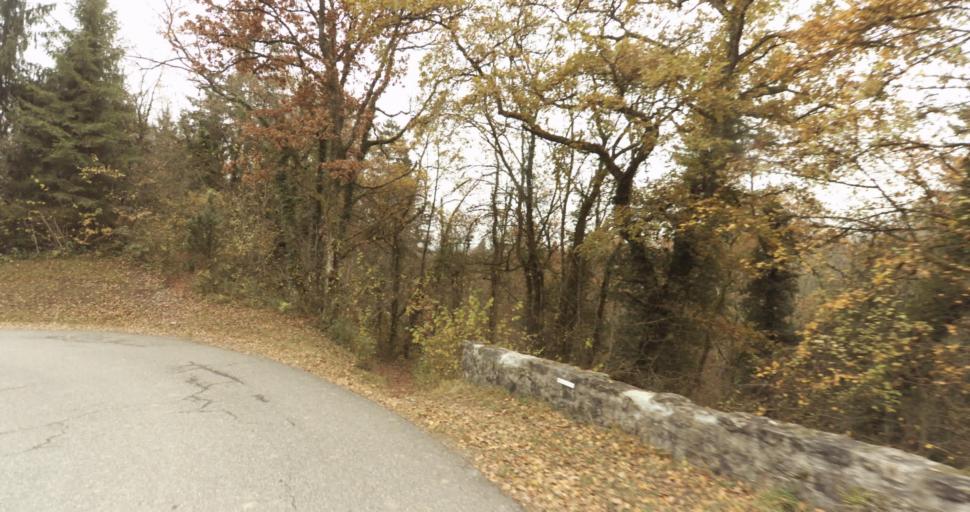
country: FR
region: Rhone-Alpes
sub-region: Departement de la Haute-Savoie
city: Lovagny
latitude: 45.9059
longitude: 6.0521
